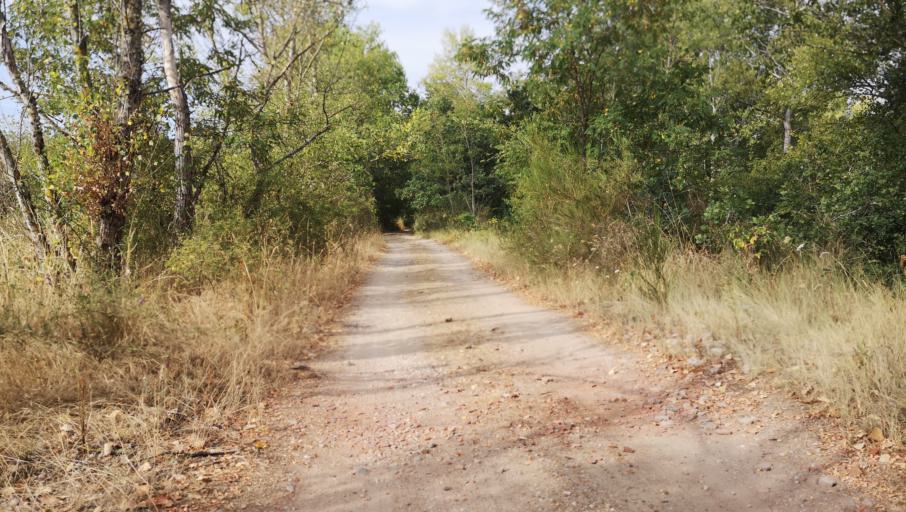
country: FR
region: Centre
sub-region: Departement du Loiret
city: Sandillon
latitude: 47.8604
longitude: 2.0364
